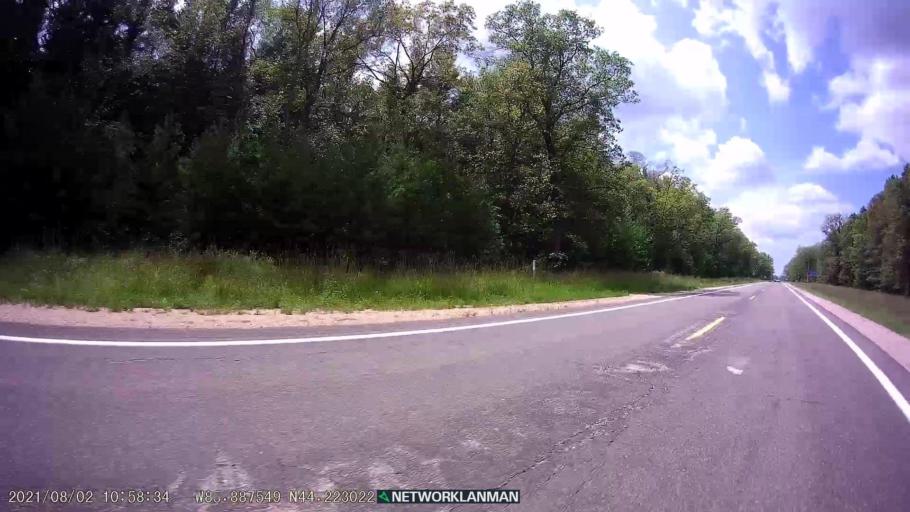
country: US
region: Michigan
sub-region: Lake County
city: Baldwin
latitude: 44.2230
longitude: -85.8883
